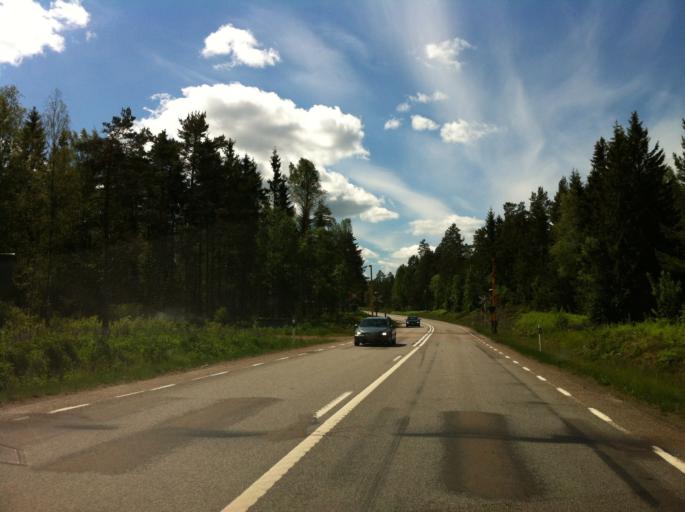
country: SE
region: Vaestra Goetaland
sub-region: Amals Kommun
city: Amal
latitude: 59.0388
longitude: 12.6735
